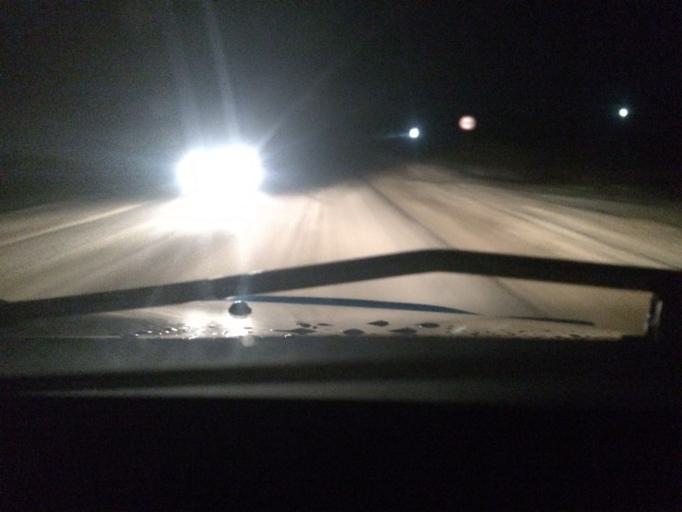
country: RU
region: Tula
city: Krapivna
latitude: 54.1171
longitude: 37.2234
